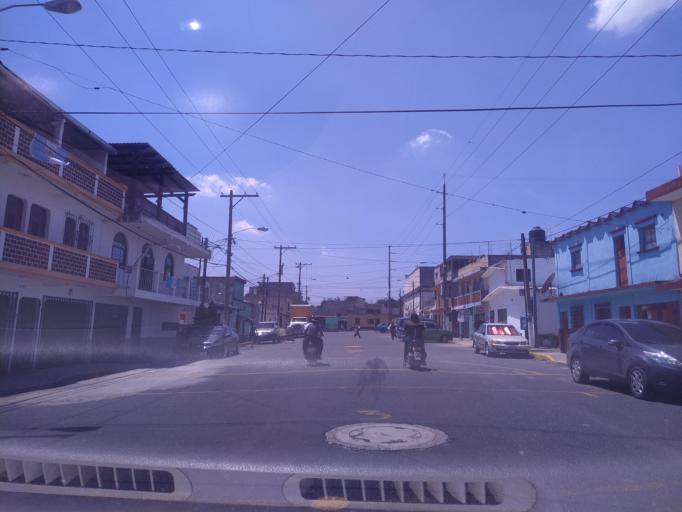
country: GT
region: Guatemala
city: Mixco
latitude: 14.6787
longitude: -90.5704
